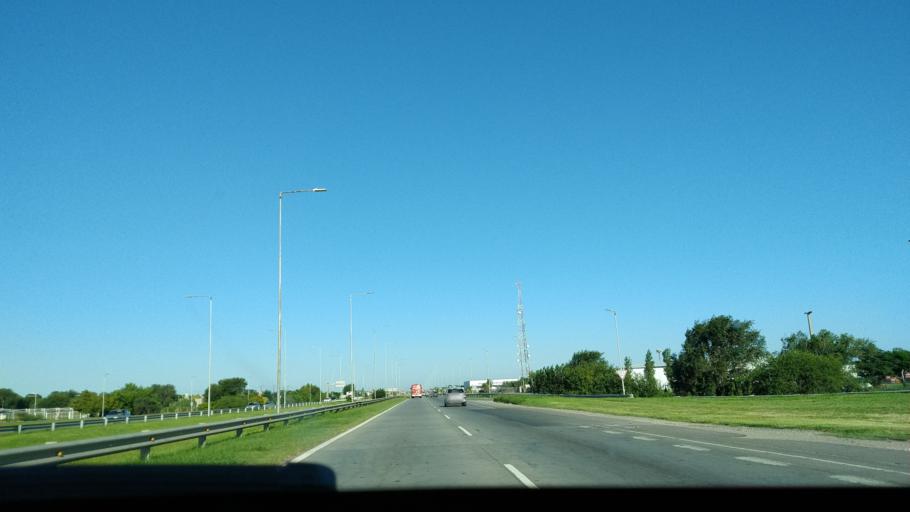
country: AR
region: Cordoba
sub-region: Departamento de Capital
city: Cordoba
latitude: -31.3579
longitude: -64.1746
